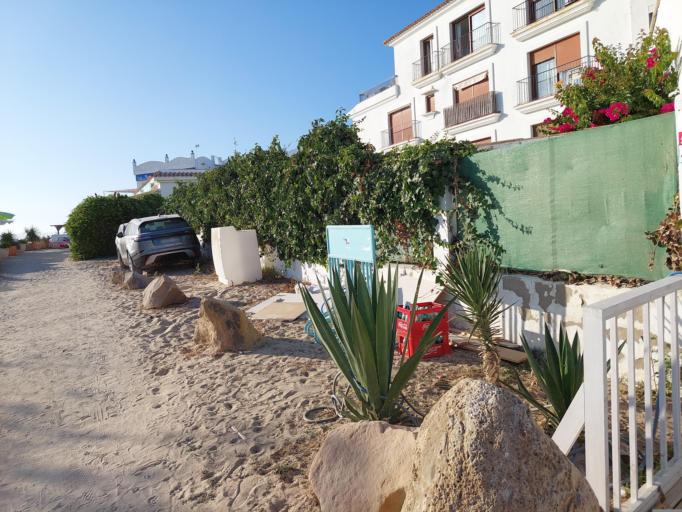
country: ES
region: Andalusia
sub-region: Provincia de Cadiz
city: Zahara de los Atunes
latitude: 36.1371
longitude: -5.8492
